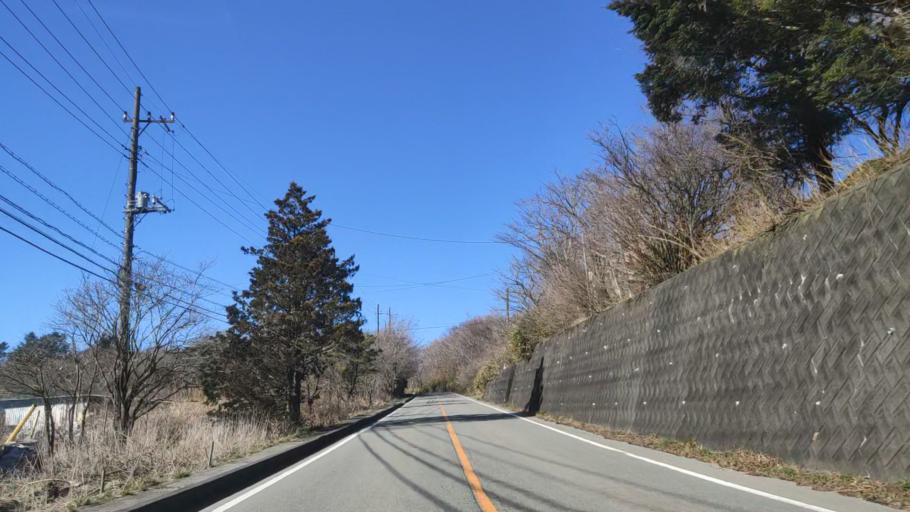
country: JP
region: Yamanashi
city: Fujikawaguchiko
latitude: 35.4203
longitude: 138.6243
